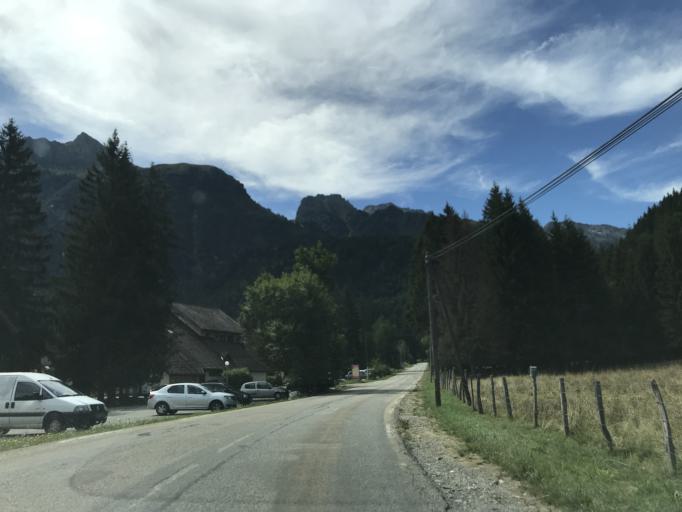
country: FR
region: Rhone-Alpes
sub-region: Departement de l'Isere
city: Theys
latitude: 45.2851
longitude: 6.0749
